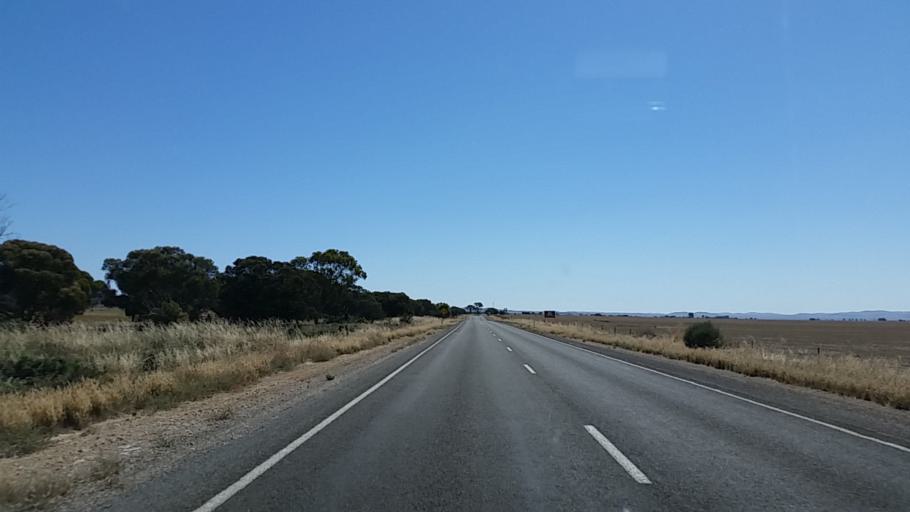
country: AU
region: South Australia
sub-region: Peterborough
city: Peterborough
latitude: -32.7536
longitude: 138.6434
